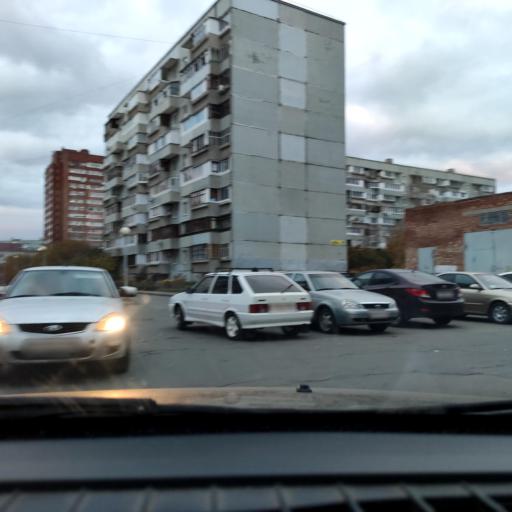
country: RU
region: Samara
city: Tol'yatti
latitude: 53.5386
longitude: 49.3415
